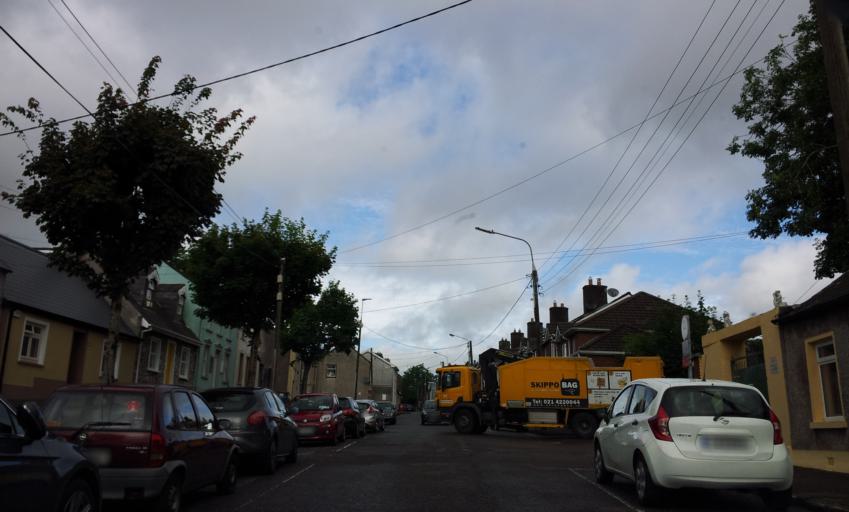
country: IE
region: Munster
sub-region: County Cork
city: Cork
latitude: 51.8906
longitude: -8.4705
